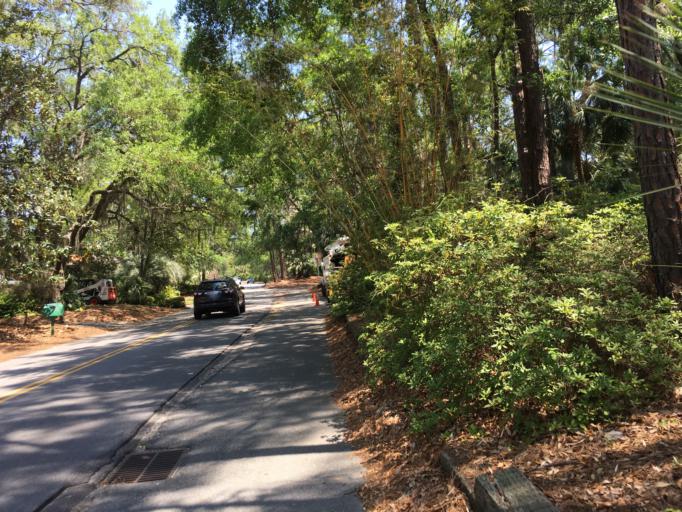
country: US
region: Georgia
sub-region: Chatham County
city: Tybee Island
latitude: 32.1114
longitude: -80.8188
